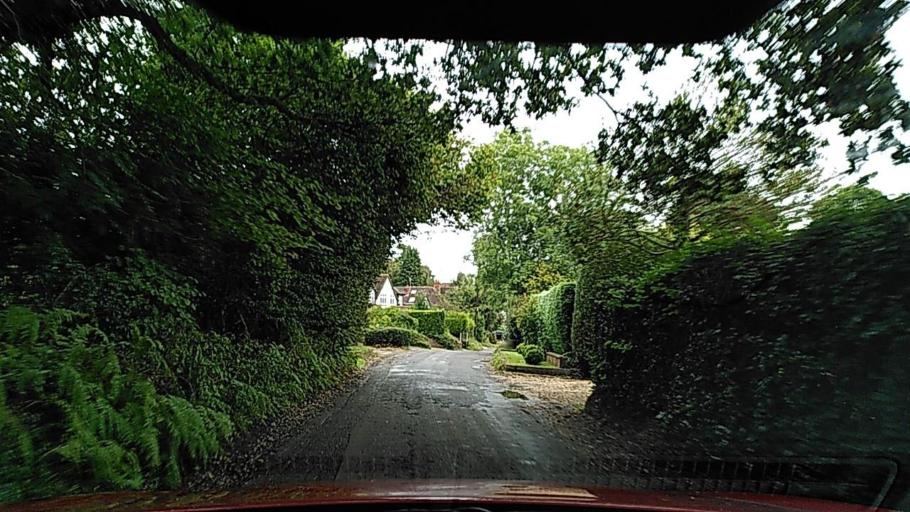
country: GB
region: England
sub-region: Oxfordshire
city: Sonning Common
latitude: 51.5129
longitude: -0.9878
